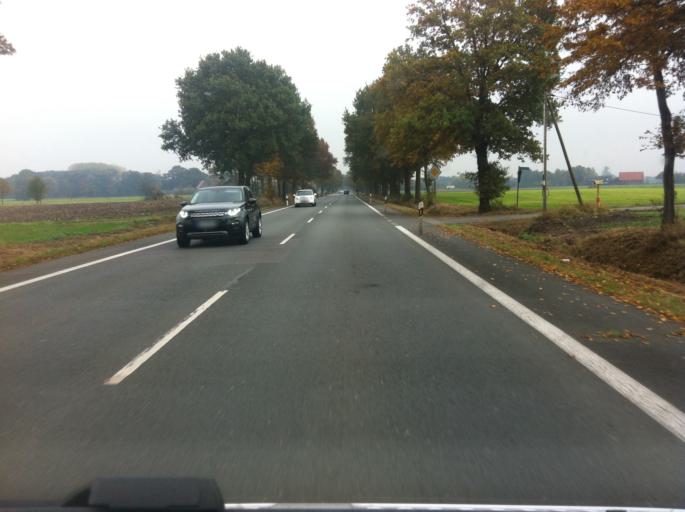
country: DE
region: North Rhine-Westphalia
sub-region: Regierungsbezirk Munster
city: Sudlohn
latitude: 51.9327
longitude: 6.8287
